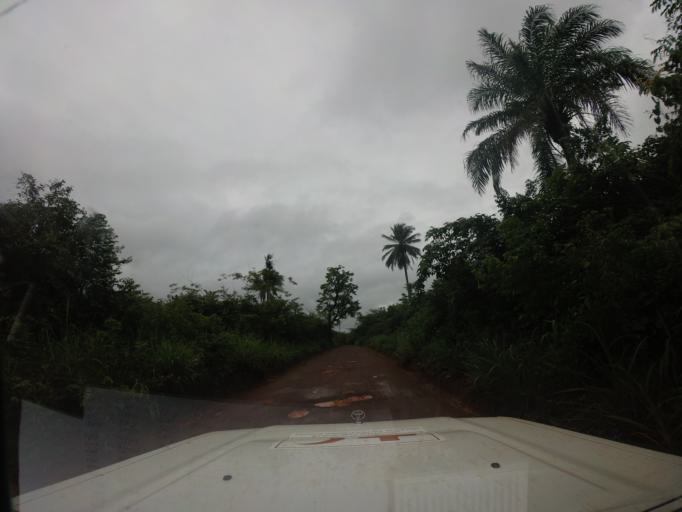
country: SL
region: Northern Province
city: Kambia
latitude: 9.1543
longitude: -12.8790
